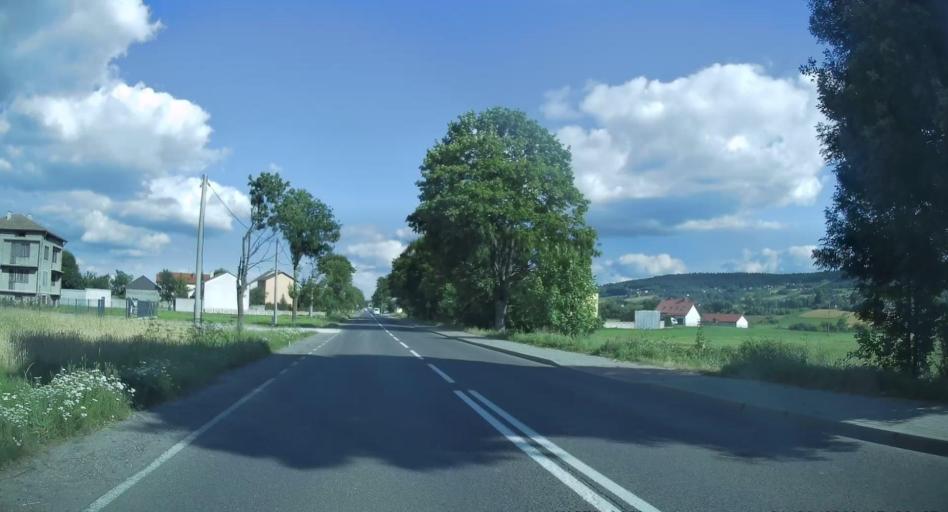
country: PL
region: Swietokrzyskie
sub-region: Powiat kielecki
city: Bodzentyn
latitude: 50.9485
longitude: 20.9323
